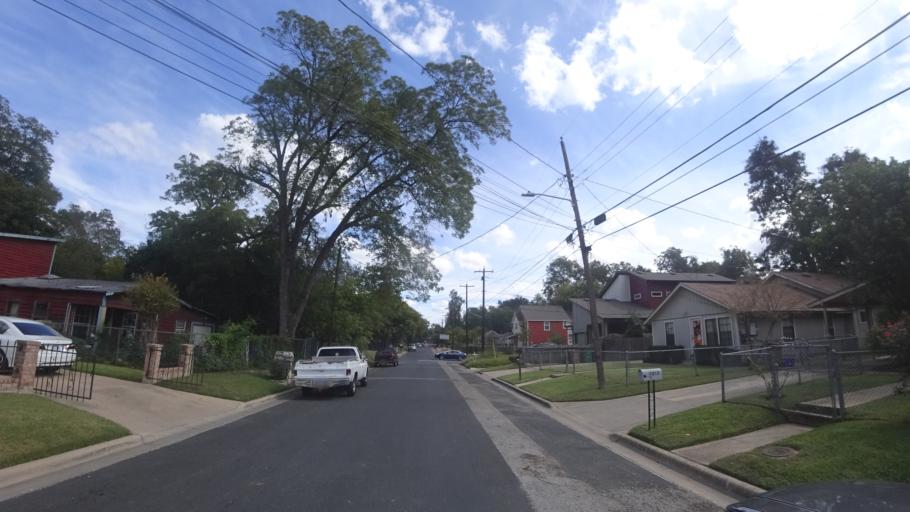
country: US
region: Texas
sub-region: Travis County
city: Austin
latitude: 30.2614
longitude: -97.7072
